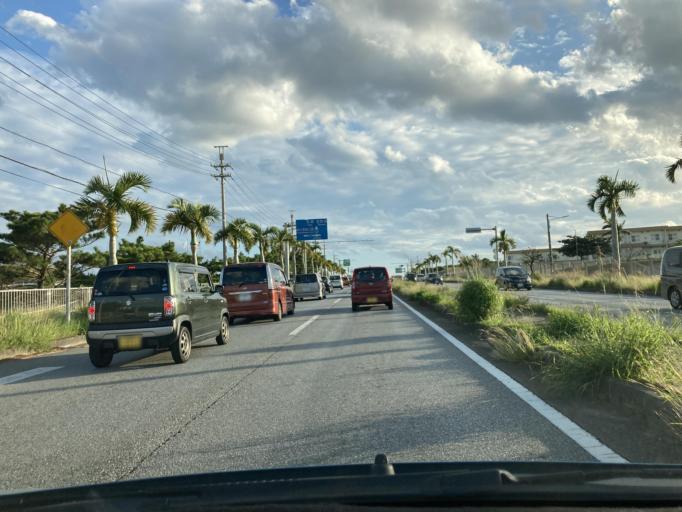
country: JP
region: Okinawa
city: Chatan
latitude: 26.2998
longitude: 127.7806
